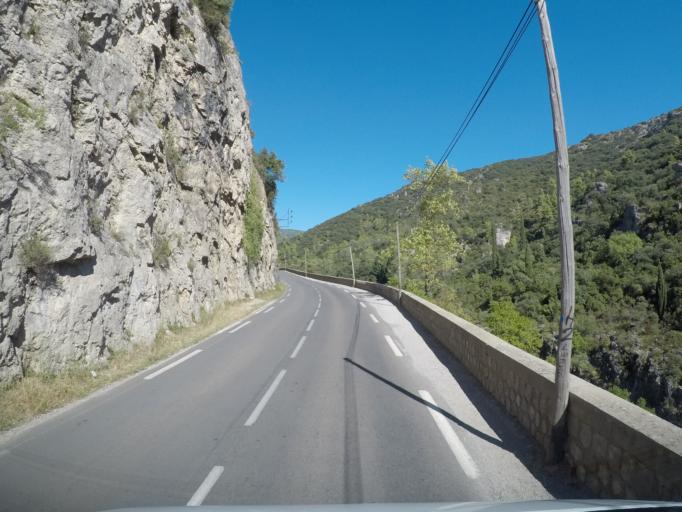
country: FR
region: Languedoc-Roussillon
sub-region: Departement de l'Herault
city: Saint-Jean-de-Fos
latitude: 43.7203
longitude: 3.5535
